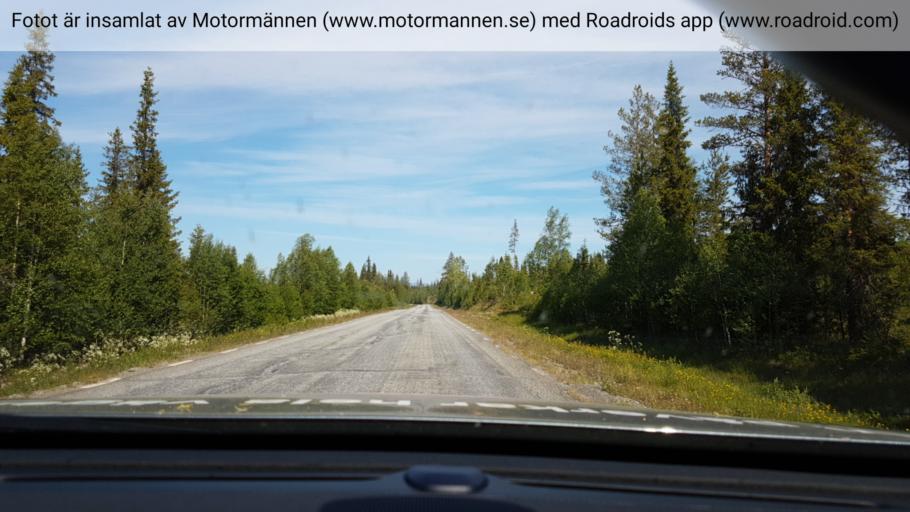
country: SE
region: Vaesterbotten
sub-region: Vilhelmina Kommun
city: Sjoberg
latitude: 64.5987
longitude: 15.8659
